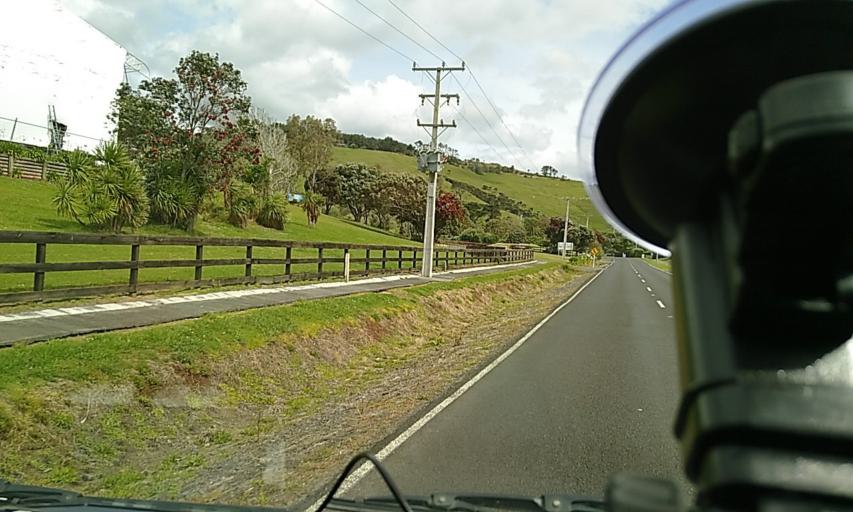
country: NZ
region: Northland
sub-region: Far North District
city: Ahipara
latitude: -35.5286
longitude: 173.3899
